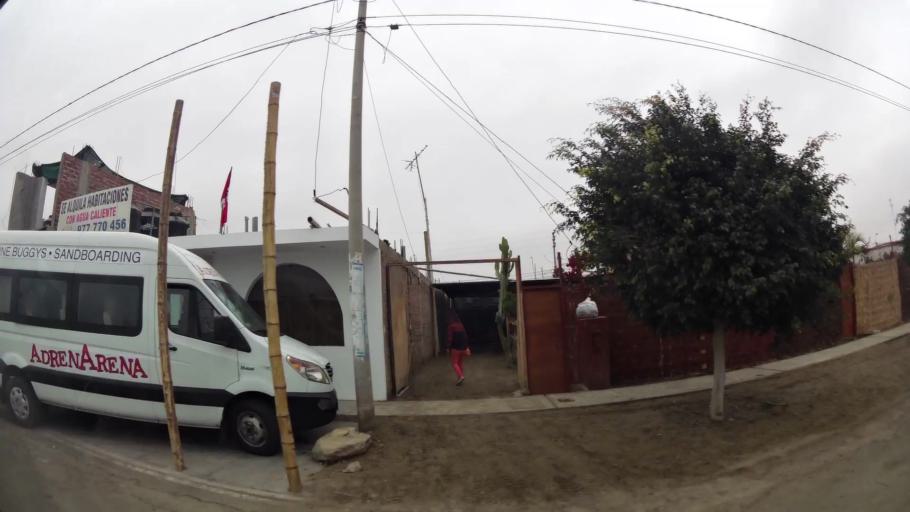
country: PE
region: Ica
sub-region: Provincia de Pisco
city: Paracas
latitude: -13.8367
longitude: -76.2488
